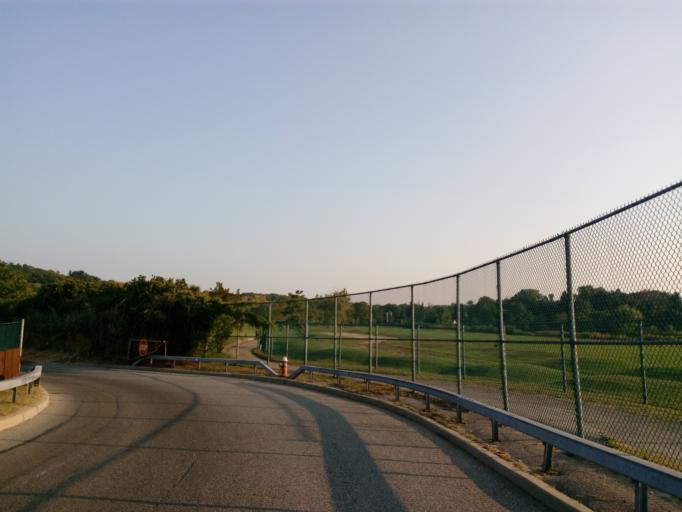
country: US
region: New York
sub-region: Nassau County
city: Lattingtown
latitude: 40.8975
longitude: -73.6203
